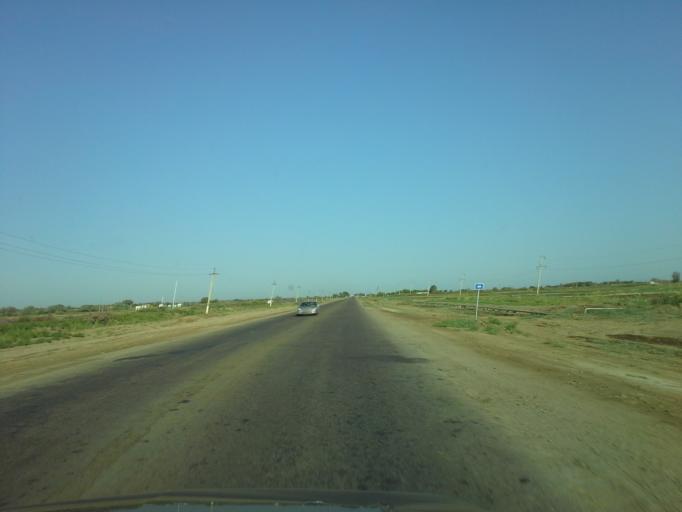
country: UZ
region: Karakalpakstan
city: Khujayli
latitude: 42.2255
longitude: 59.4777
